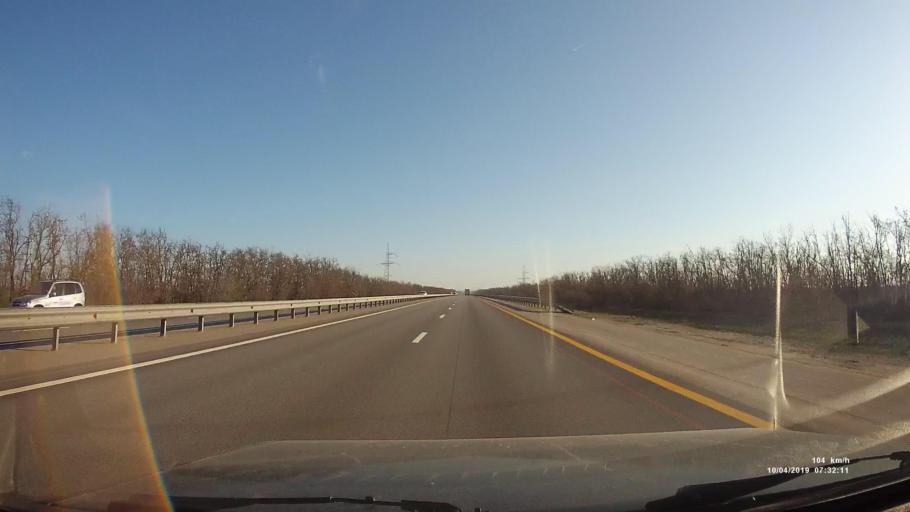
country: RU
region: Rostov
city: Zverevo
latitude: 47.9952
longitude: 40.2283
